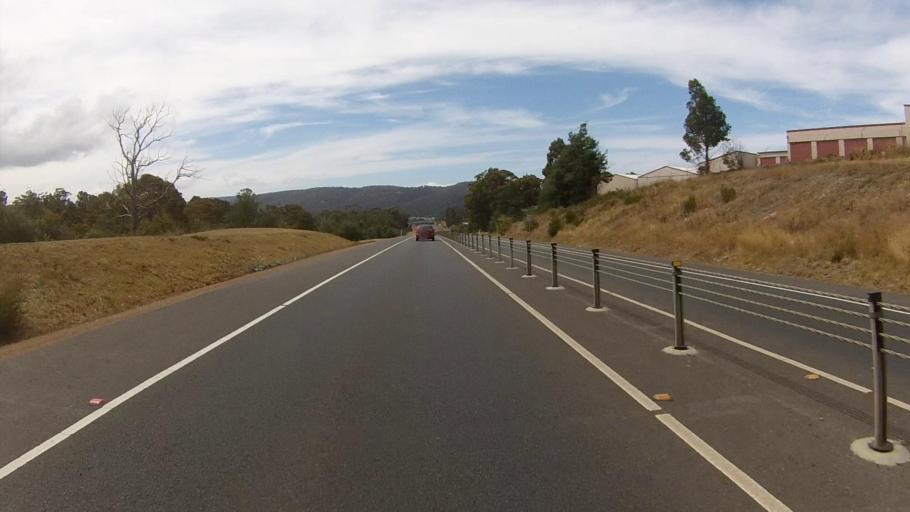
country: AU
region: Tasmania
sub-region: Kingborough
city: Kingston
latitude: -42.9813
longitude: 147.2920
